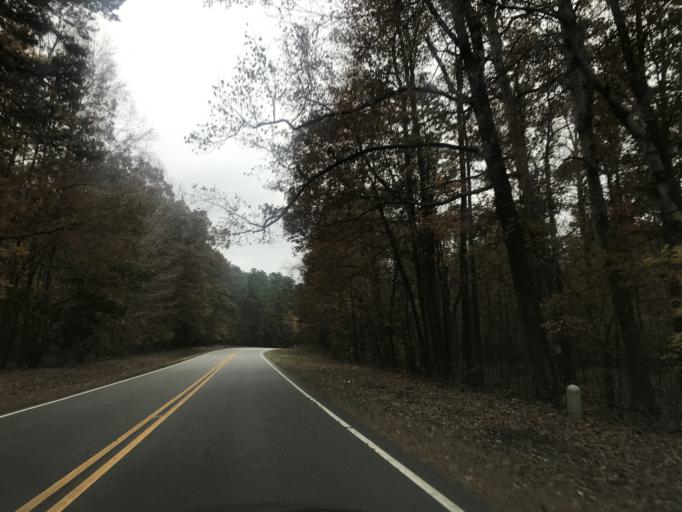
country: US
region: North Carolina
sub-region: Franklin County
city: Youngsville
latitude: 36.0085
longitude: -78.4905
